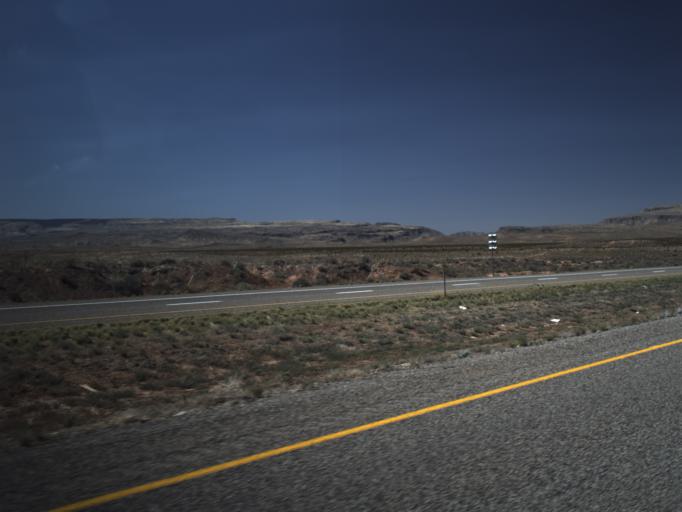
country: US
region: Utah
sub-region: Washington County
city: Saint George
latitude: 37.0013
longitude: -113.5748
